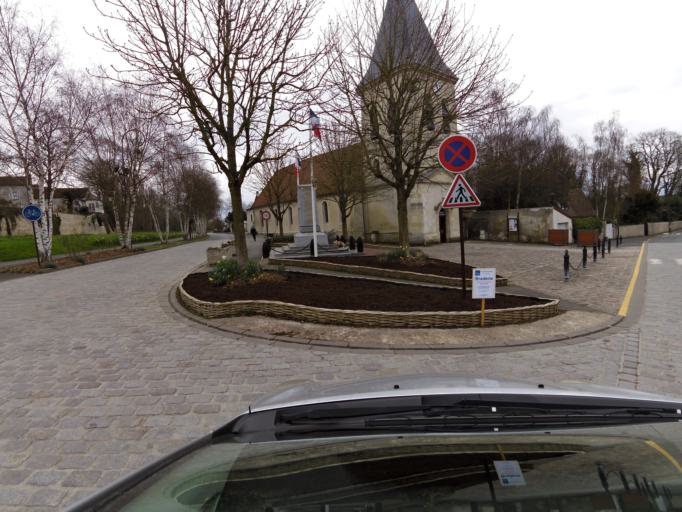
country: FR
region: Ile-de-France
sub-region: Departement de Seine-et-Marne
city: Claye-Souilly
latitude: 48.9452
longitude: 2.6907
